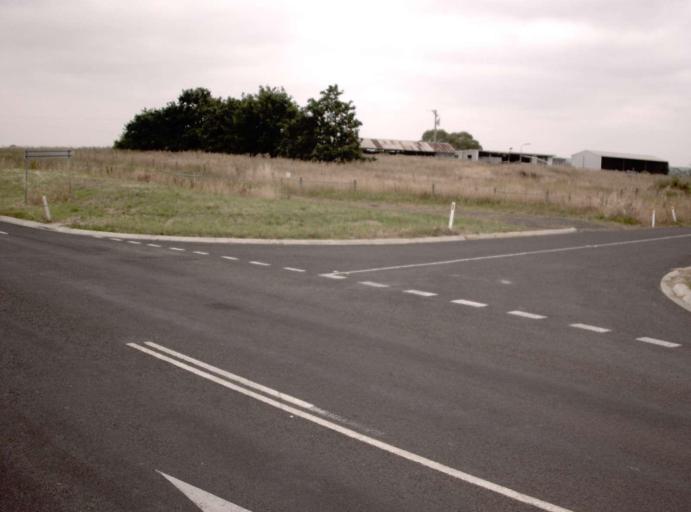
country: AU
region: Victoria
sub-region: Latrobe
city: Morwell
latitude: -38.2609
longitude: 146.3303
